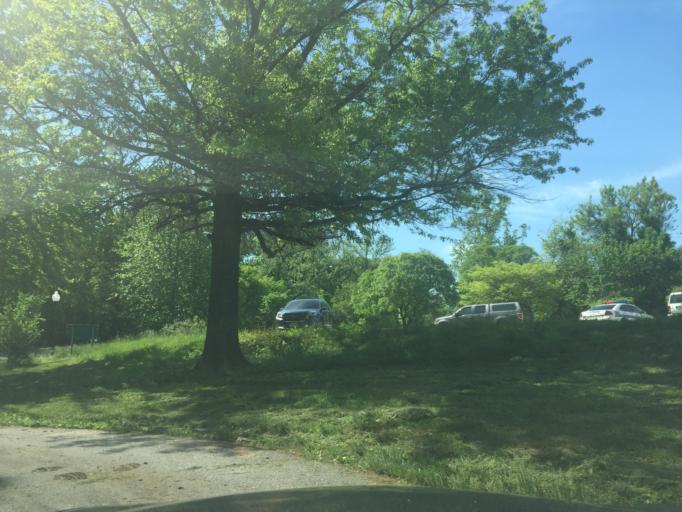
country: US
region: Maryland
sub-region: City of Baltimore
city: Baltimore
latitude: 39.3236
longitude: -76.6434
